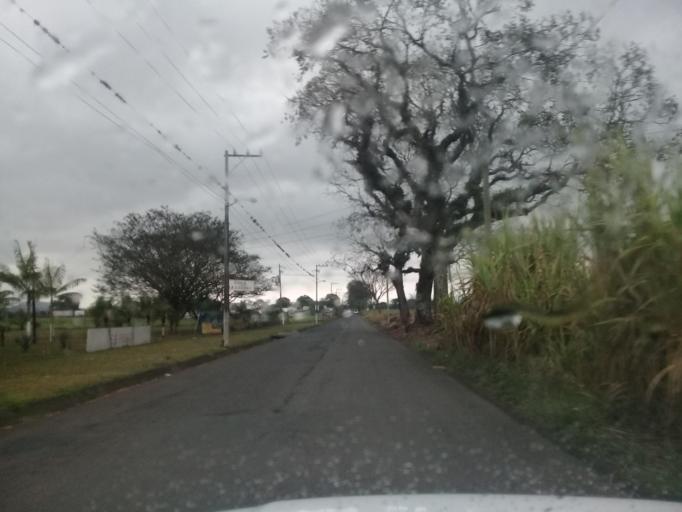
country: MX
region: Veracruz
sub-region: Cordoba
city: San Jose de Tapia
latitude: 18.8536
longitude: -96.9507
